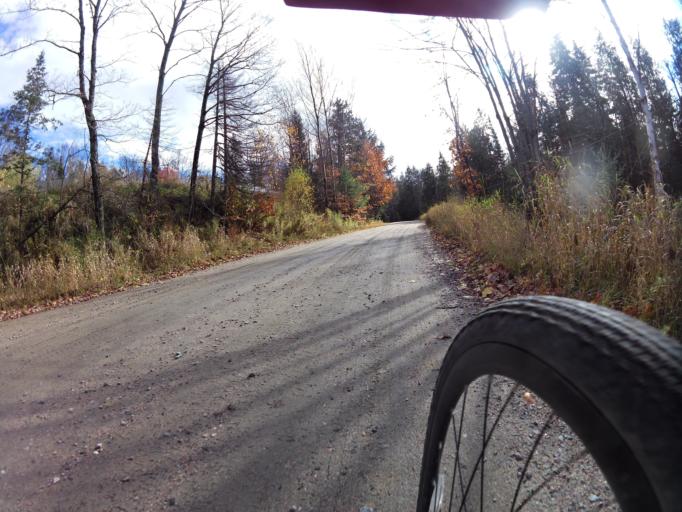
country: CA
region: Quebec
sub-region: Outaouais
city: Wakefield
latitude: 45.7297
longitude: -76.0314
